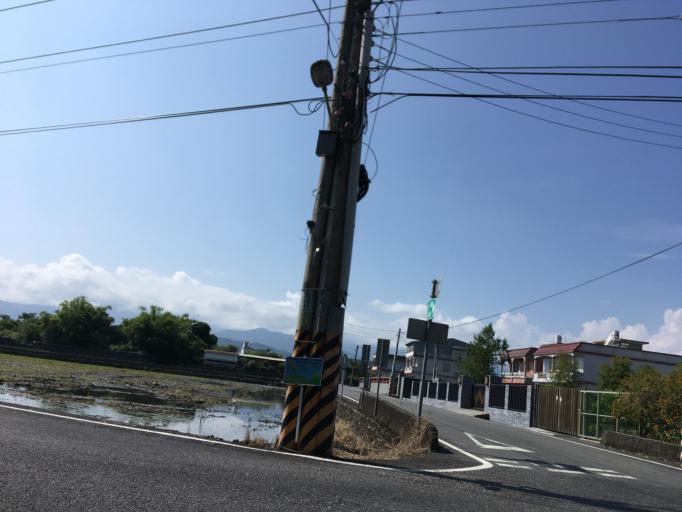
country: TW
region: Taiwan
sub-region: Yilan
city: Yilan
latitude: 24.6763
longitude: 121.7308
